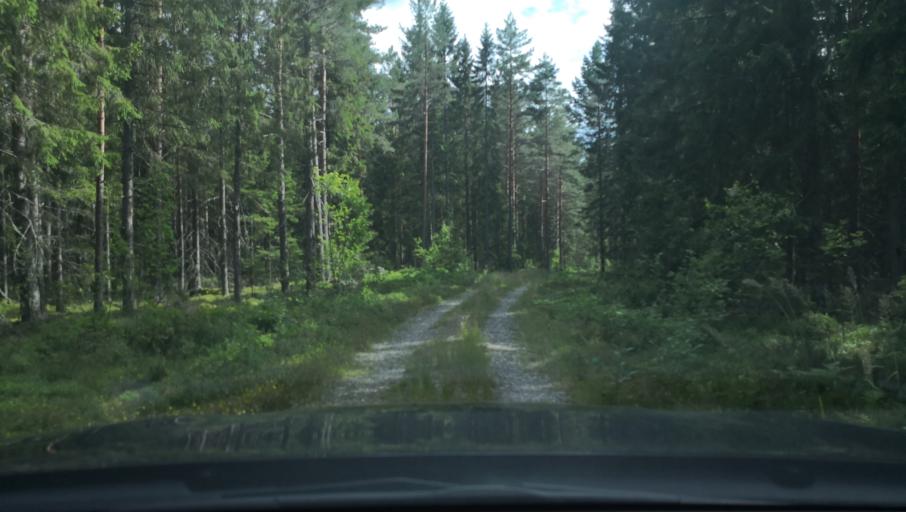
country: SE
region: Vaestmanland
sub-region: Surahammars Kommun
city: Surahammar
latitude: 59.6529
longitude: 16.0978
